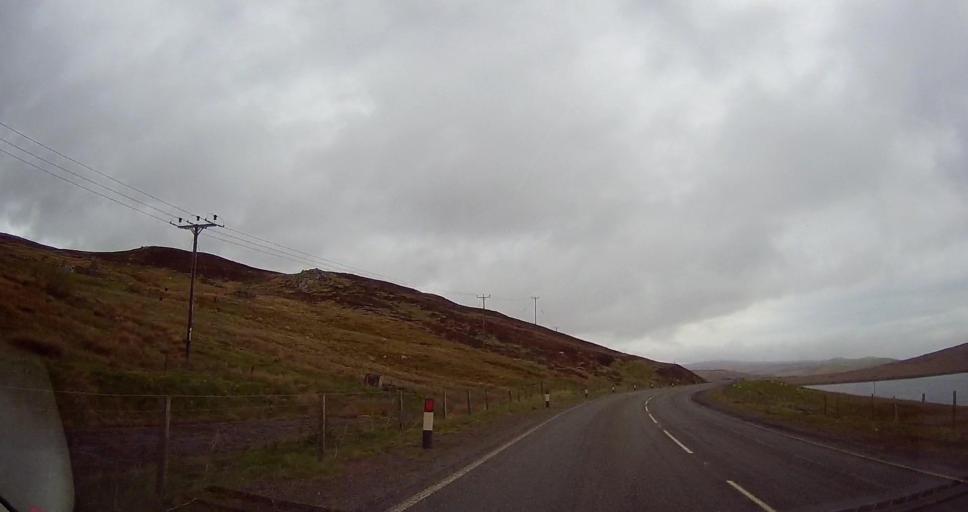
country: GB
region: Scotland
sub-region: Shetland Islands
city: Lerwick
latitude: 60.2558
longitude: -1.2266
